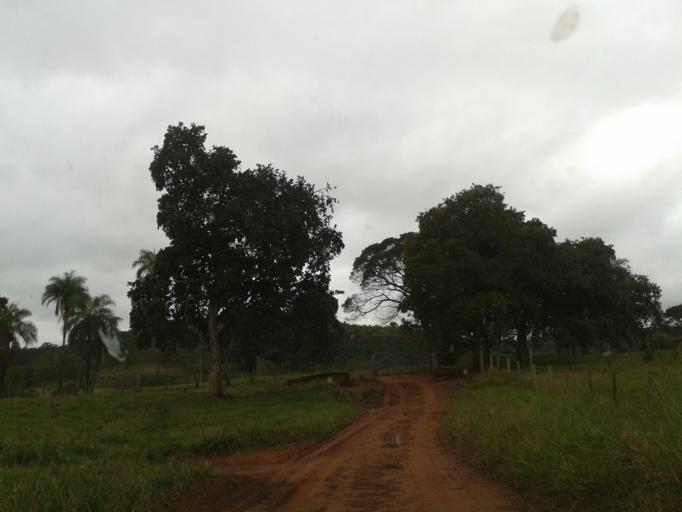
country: BR
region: Minas Gerais
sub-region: Campina Verde
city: Campina Verde
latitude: -19.4675
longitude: -49.5842
